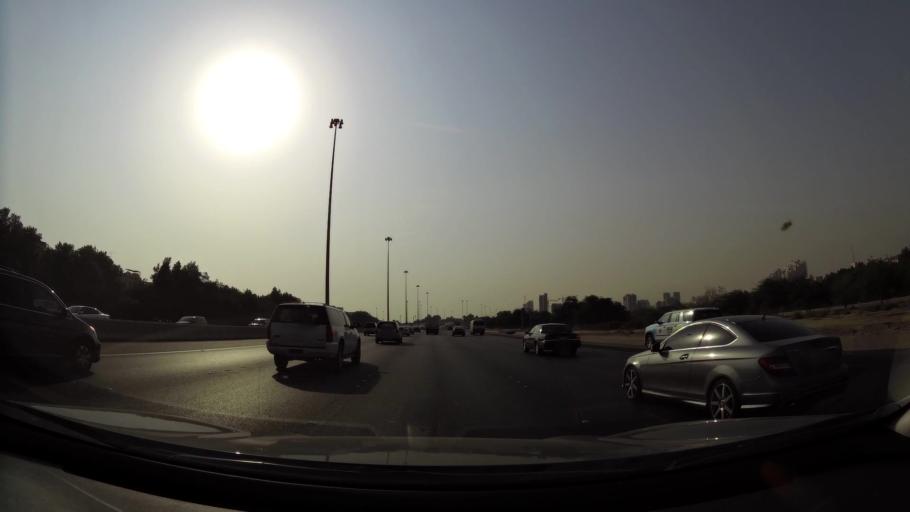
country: KW
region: Muhafazat Hawalli
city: Salwa
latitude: 29.2753
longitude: 48.0815
